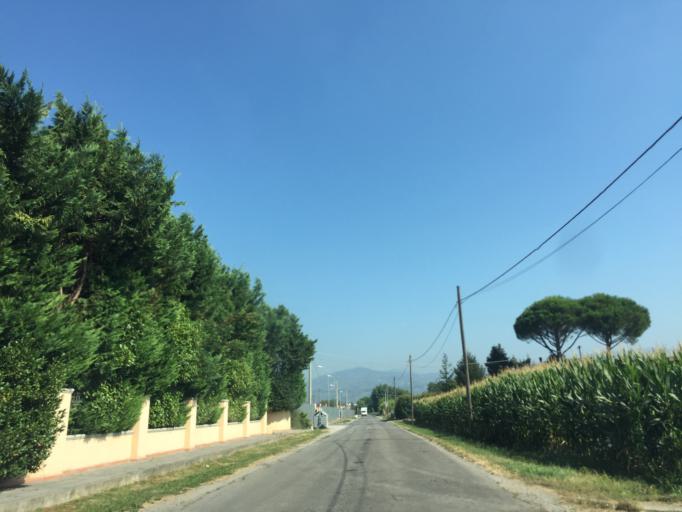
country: IT
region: Tuscany
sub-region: Provincia di Pistoia
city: Ponte Buggianese
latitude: 43.8480
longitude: 10.7424
